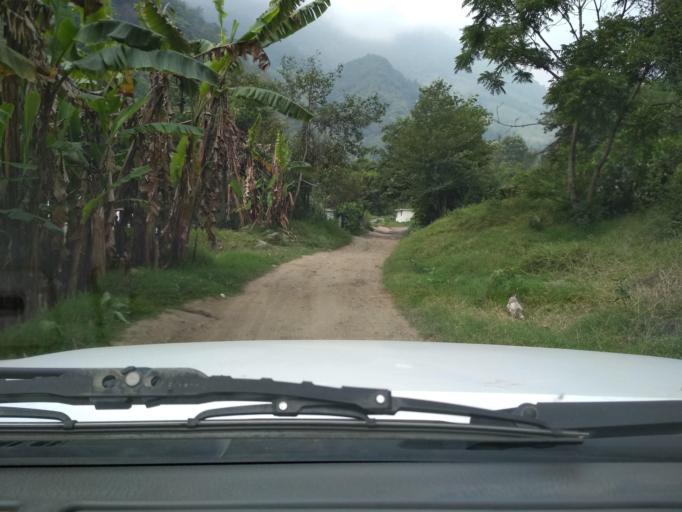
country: MX
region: Veracruz
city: Xocotla
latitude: 18.9901
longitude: -97.1084
